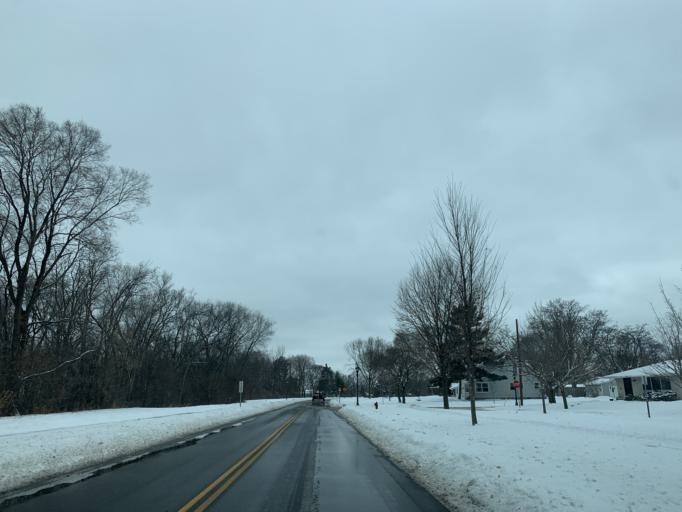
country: US
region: Minnesota
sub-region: Ramsey County
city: Roseville
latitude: 44.9870
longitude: -93.1144
